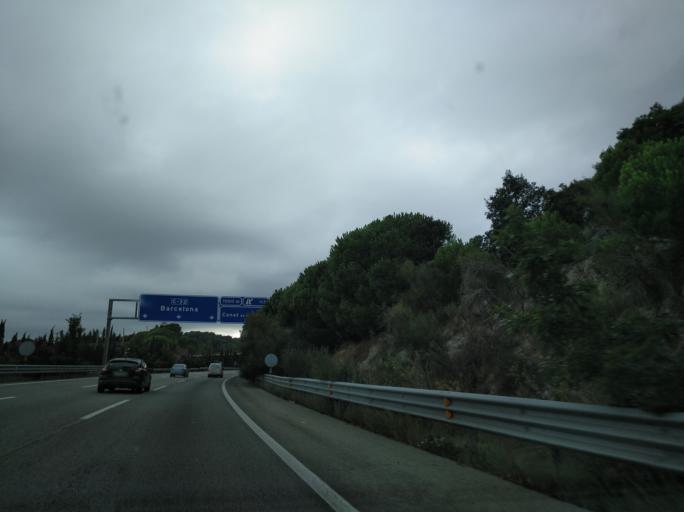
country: ES
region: Catalonia
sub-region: Provincia de Barcelona
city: Canet de Mar
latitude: 41.5998
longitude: 2.5860
